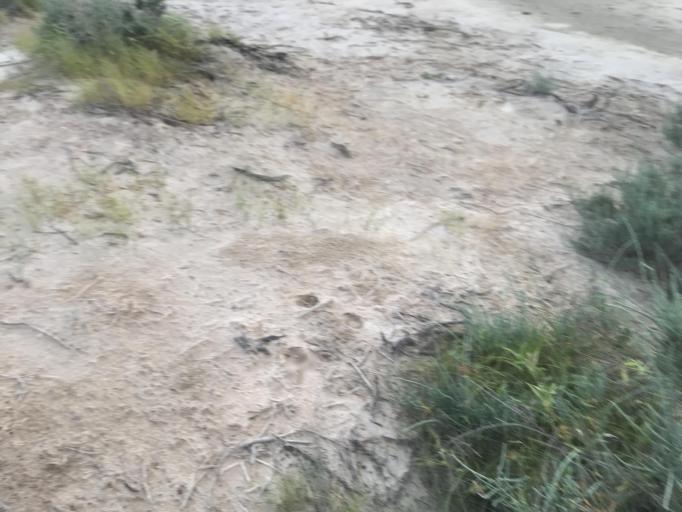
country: SN
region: Saint-Louis
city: Saint-Louis
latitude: 15.9310
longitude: -16.4618
